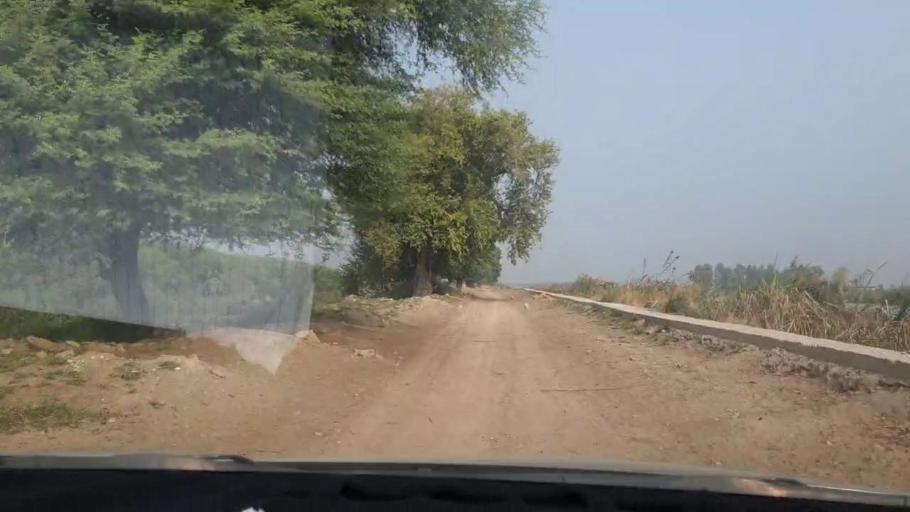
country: PK
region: Sindh
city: Matiari
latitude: 25.6731
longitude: 68.5579
